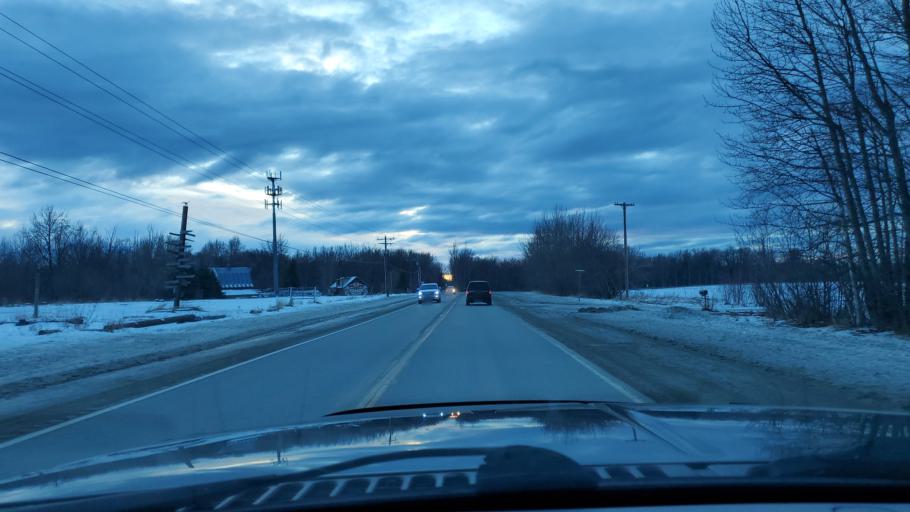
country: US
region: Alaska
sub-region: Matanuska-Susitna Borough
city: Farm Loop
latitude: 61.6592
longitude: -149.0947
